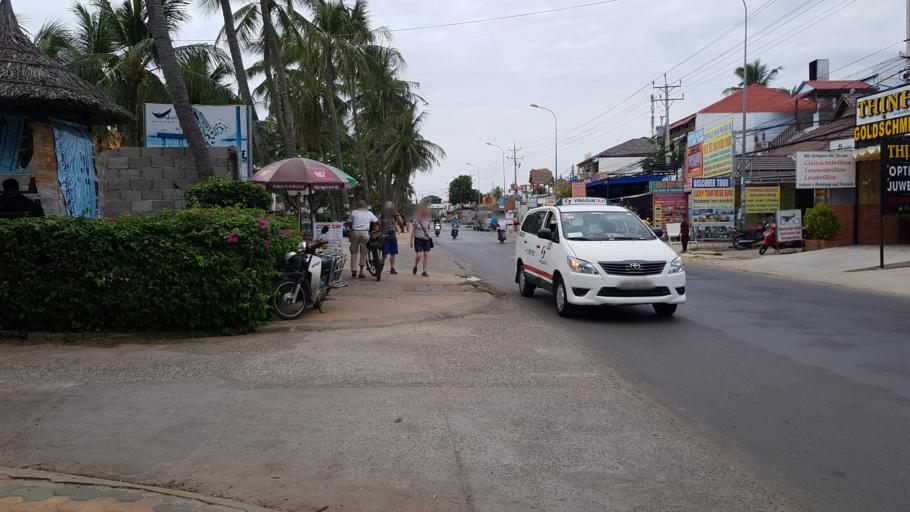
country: VN
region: Binh Thuan
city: Phan Thiet
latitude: 10.9480
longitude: 108.2032
